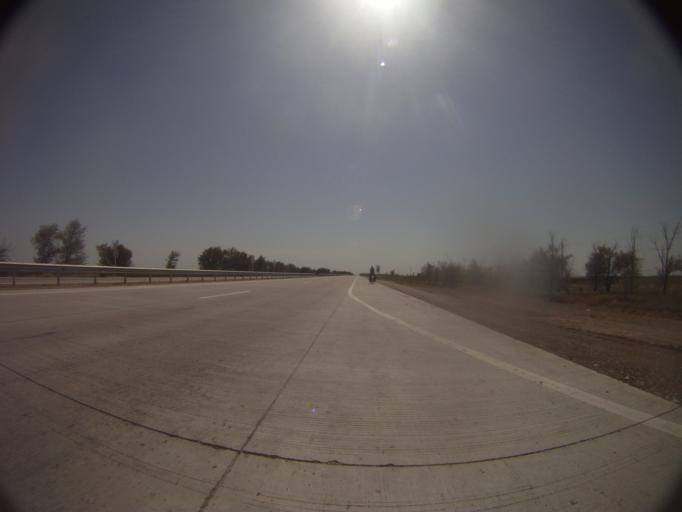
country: KZ
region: Ongtustik Qazaqstan
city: Bayaldyr
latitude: 43.0937
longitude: 68.6363
